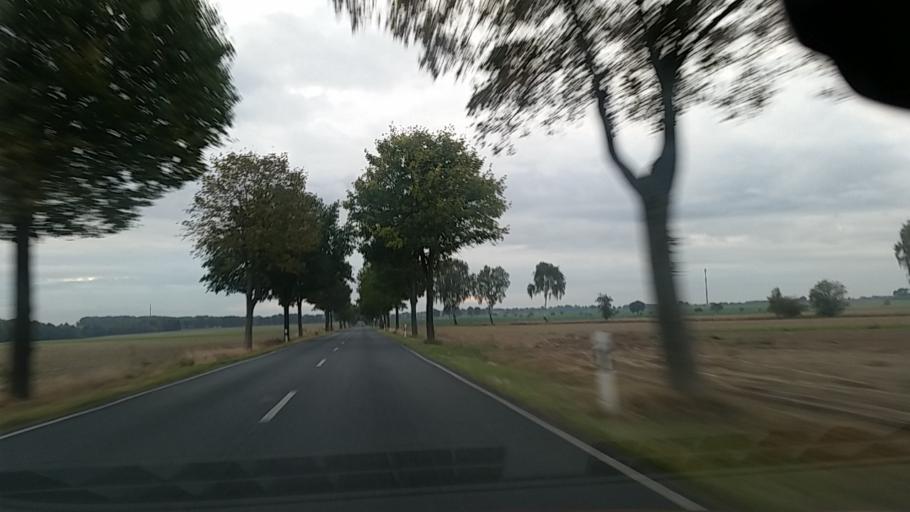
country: DE
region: Lower Saxony
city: Hankensbuttel
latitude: 52.7379
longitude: 10.5755
